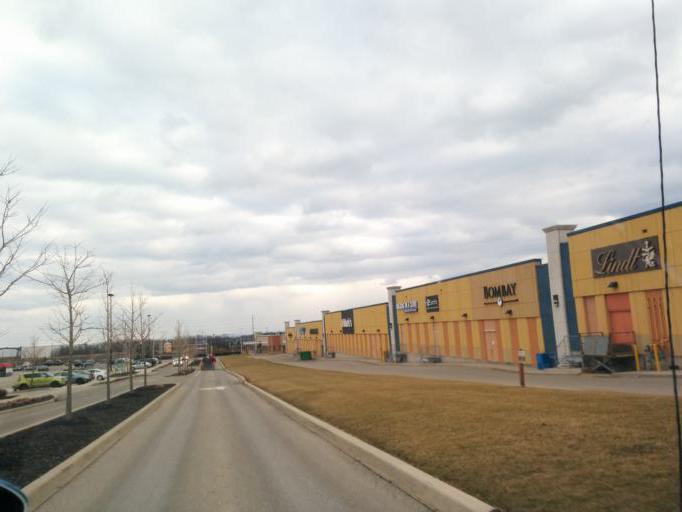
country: CA
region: Ontario
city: Oakville
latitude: 43.3982
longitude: -79.7495
